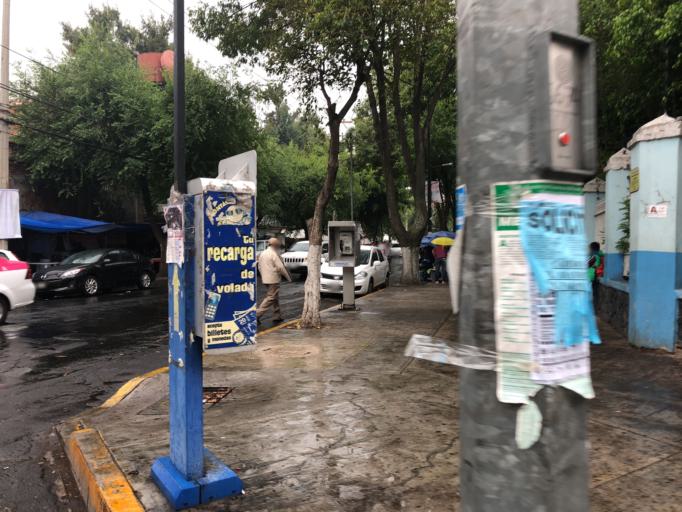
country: MX
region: Mexico City
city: Mexico City
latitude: 19.4207
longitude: -99.1487
